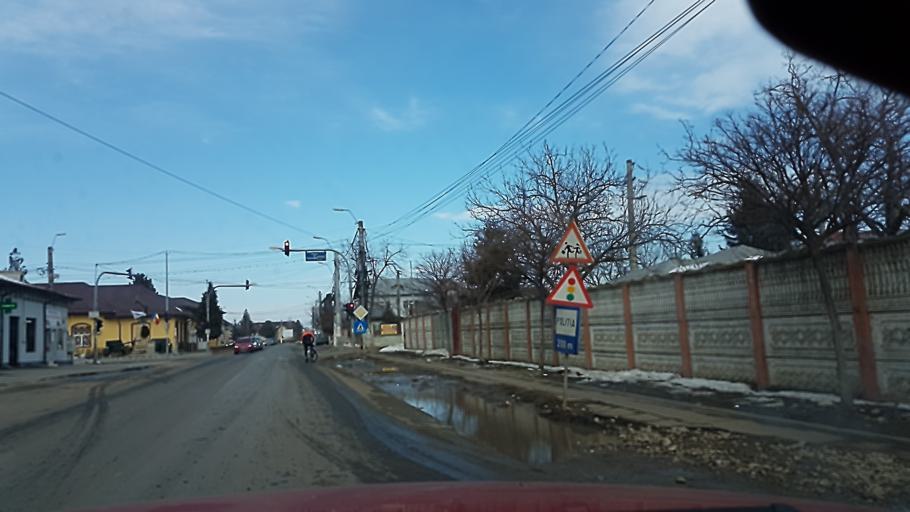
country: RO
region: Ilfov
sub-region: Comuna Tunari
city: Tunari
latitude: 44.5484
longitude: 26.1414
